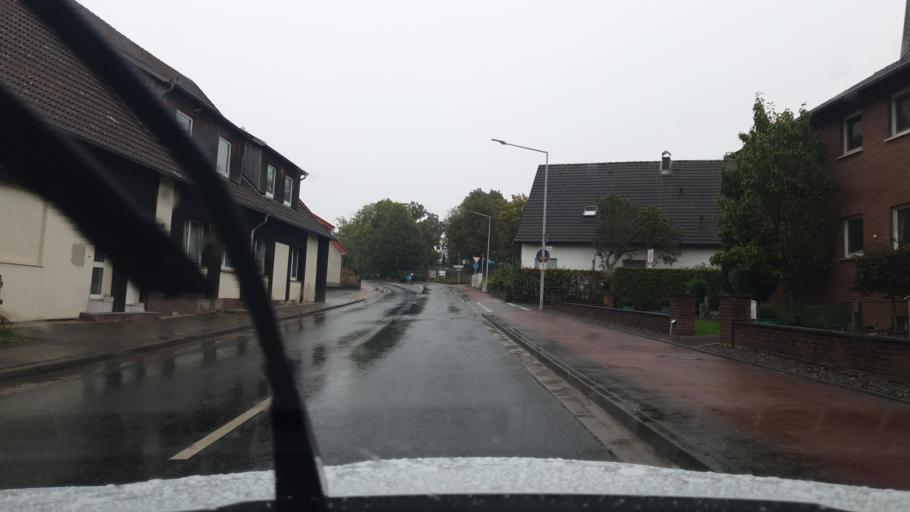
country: DE
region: North Rhine-Westphalia
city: Porta Westfalica
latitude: 52.2053
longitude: 8.9246
